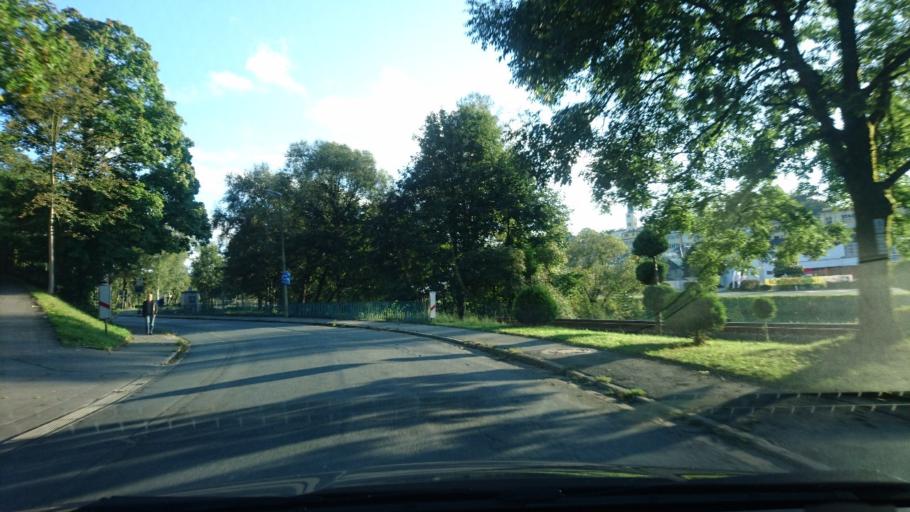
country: DE
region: Bavaria
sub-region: Upper Franconia
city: Naila
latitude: 50.3350
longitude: 11.7087
